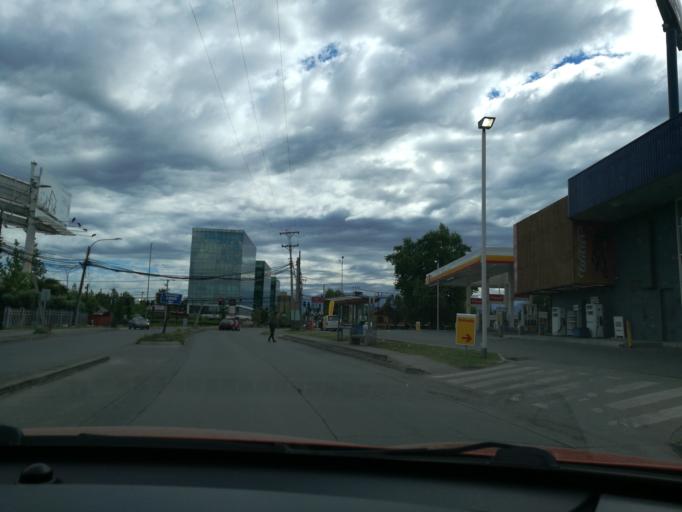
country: CL
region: O'Higgins
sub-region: Provincia de Cachapoal
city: Rancagua
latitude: -34.1821
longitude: -70.7299
